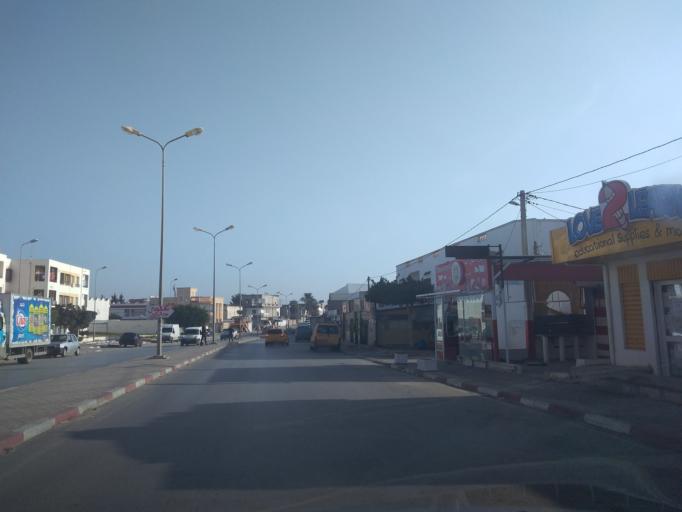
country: TN
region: Manouba
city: Manouba
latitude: 36.7884
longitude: 10.0856
